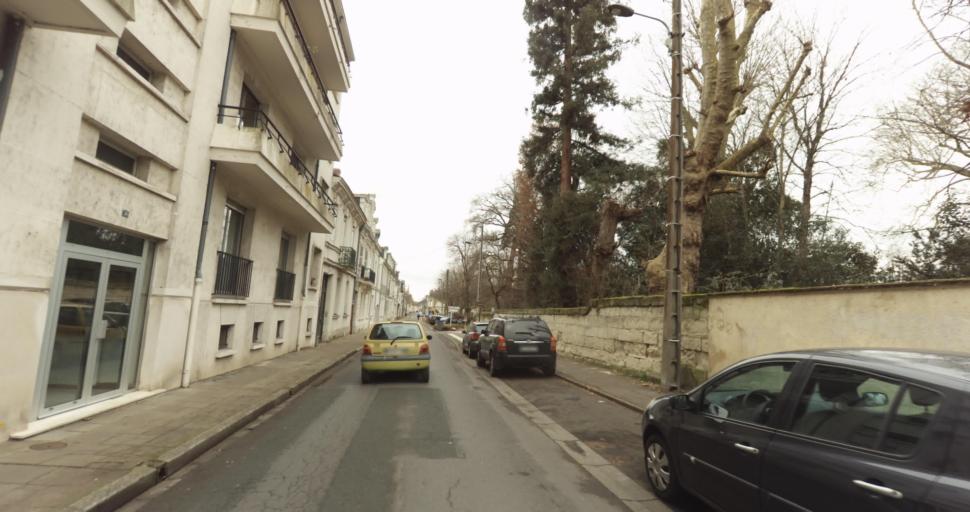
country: FR
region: Pays de la Loire
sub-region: Departement de Maine-et-Loire
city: Saumur
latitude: 47.2566
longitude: -0.0809
